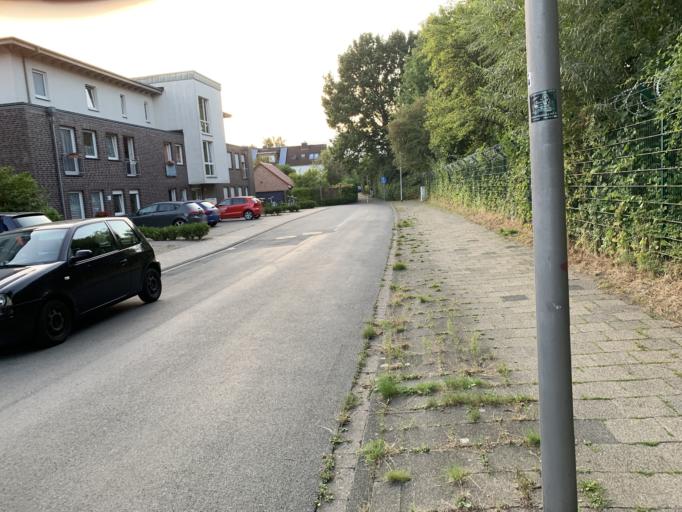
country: DE
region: North Rhine-Westphalia
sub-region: Regierungsbezirk Munster
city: Muenster
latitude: 51.9389
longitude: 7.6039
